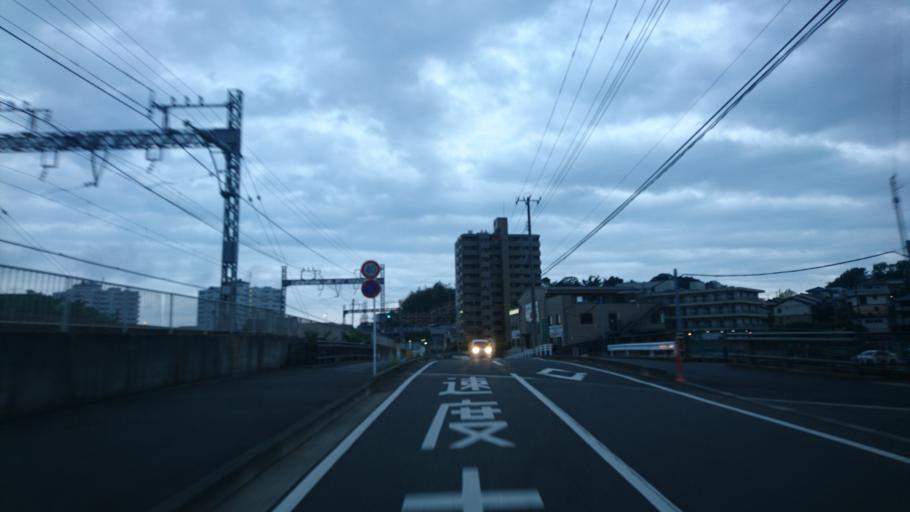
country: JP
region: Kanagawa
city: Fujisawa
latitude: 35.3526
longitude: 139.4740
